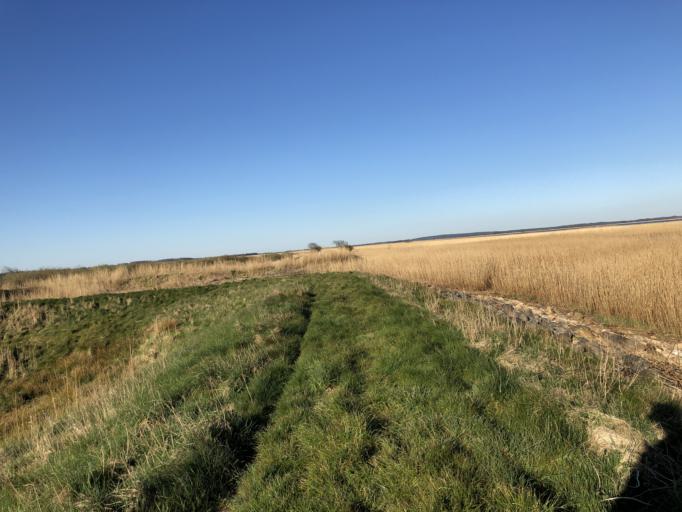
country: DK
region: Central Jutland
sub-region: Holstebro Kommune
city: Ulfborg
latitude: 56.2967
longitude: 8.2764
